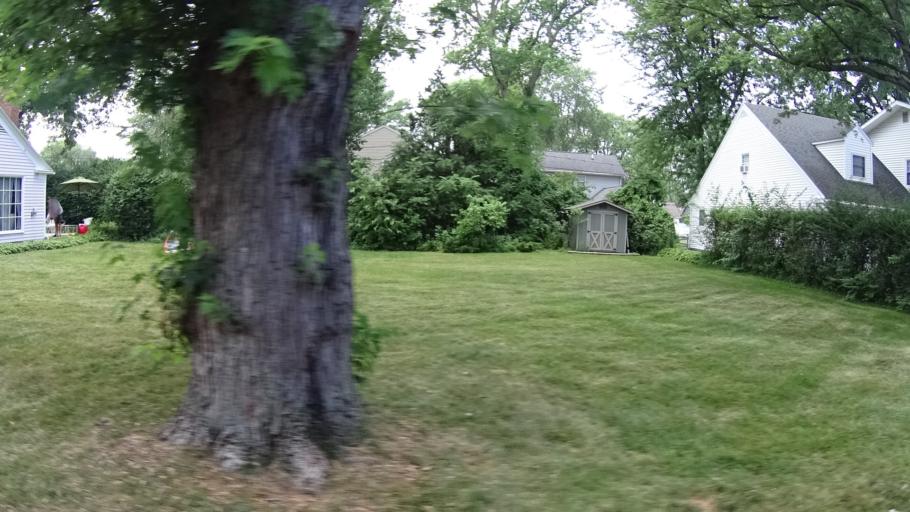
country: US
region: Ohio
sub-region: Erie County
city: Huron
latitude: 41.3917
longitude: -82.5378
